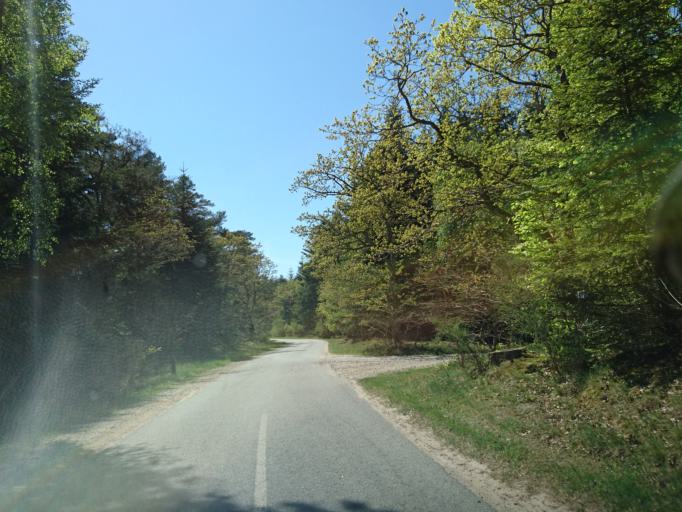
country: DK
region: North Denmark
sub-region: Hjorring Kommune
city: Sindal
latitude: 57.6013
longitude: 10.2346
